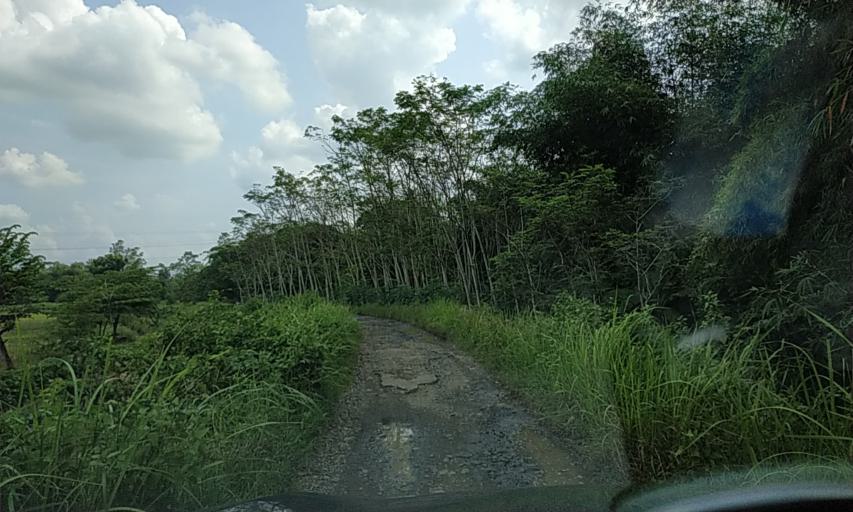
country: ID
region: Central Java
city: Sogati
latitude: -7.3369
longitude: 108.6686
